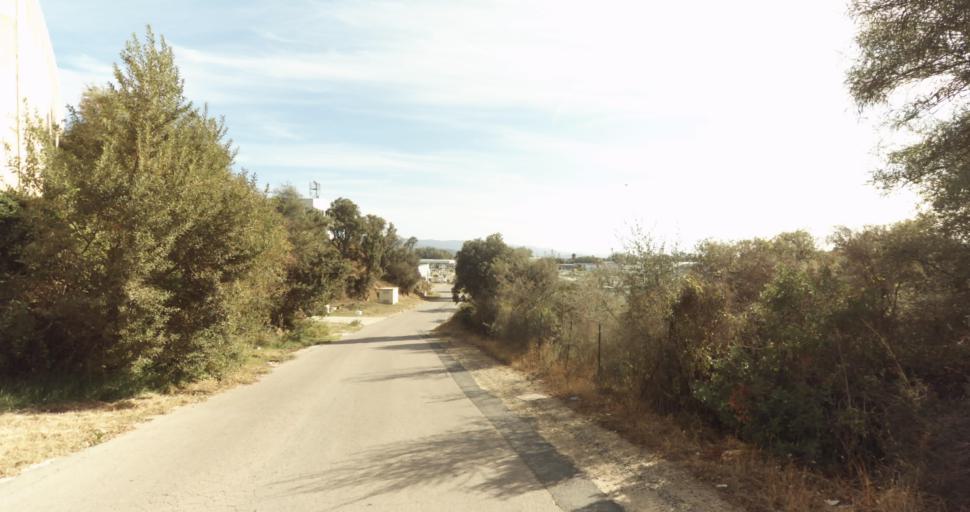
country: FR
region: Corsica
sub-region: Departement de la Corse-du-Sud
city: Afa
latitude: 41.9334
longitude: 8.7909
